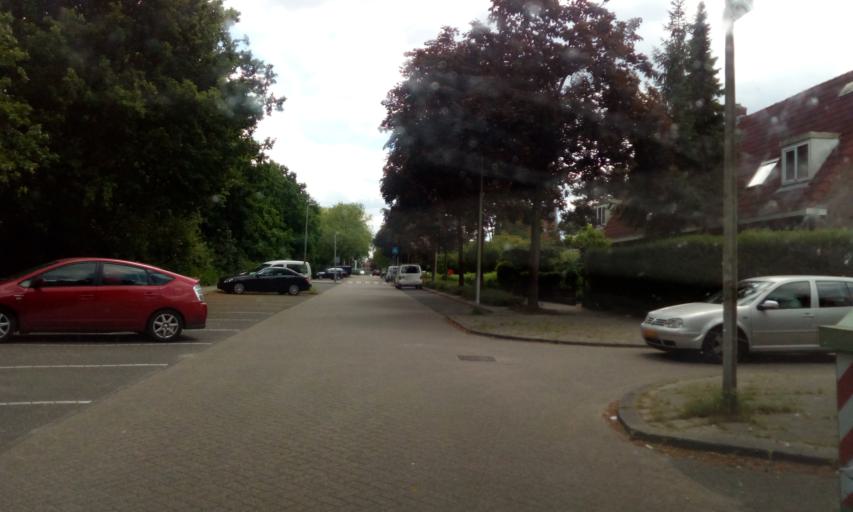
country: NL
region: North Holland
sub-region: Gemeente Bussum
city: Bussum
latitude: 52.2719
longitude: 5.1728
